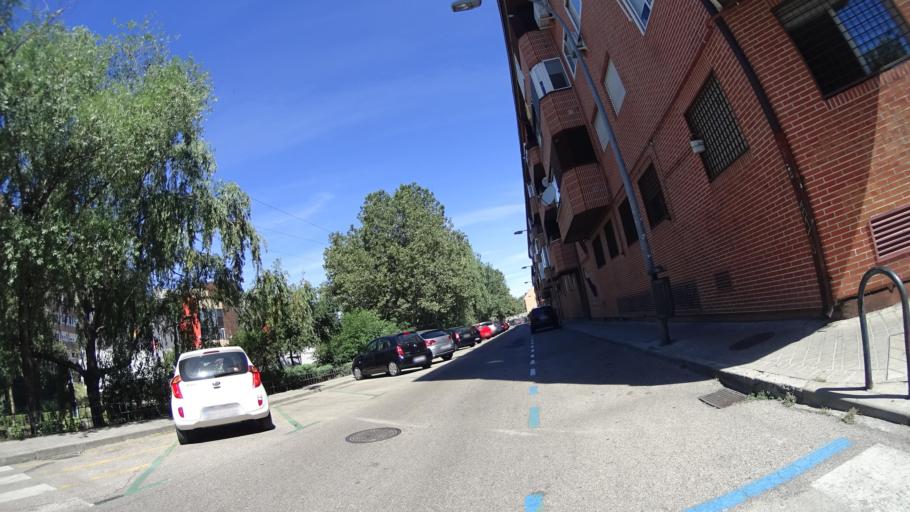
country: ES
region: Madrid
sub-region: Provincia de Madrid
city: Collado-Villalba
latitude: 40.6272
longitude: -4.0044
